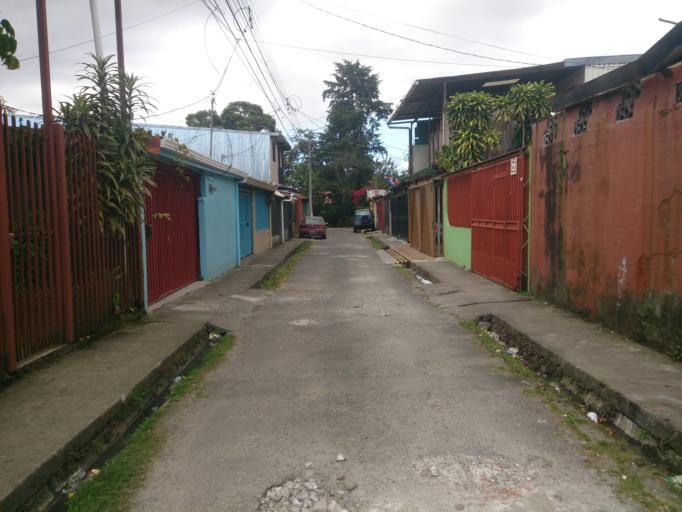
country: CR
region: Cartago
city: Concepcion
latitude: 9.9268
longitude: -84.0027
